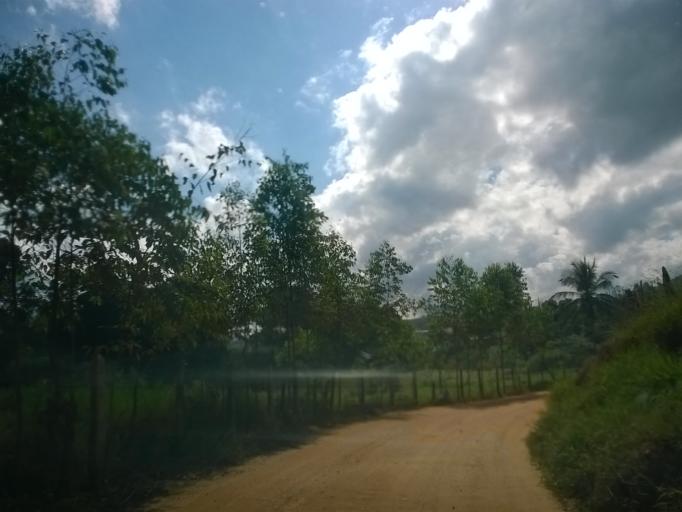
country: BR
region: Minas Gerais
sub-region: Visconde Do Rio Branco
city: Visconde do Rio Branco
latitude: -21.0500
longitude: -42.9004
